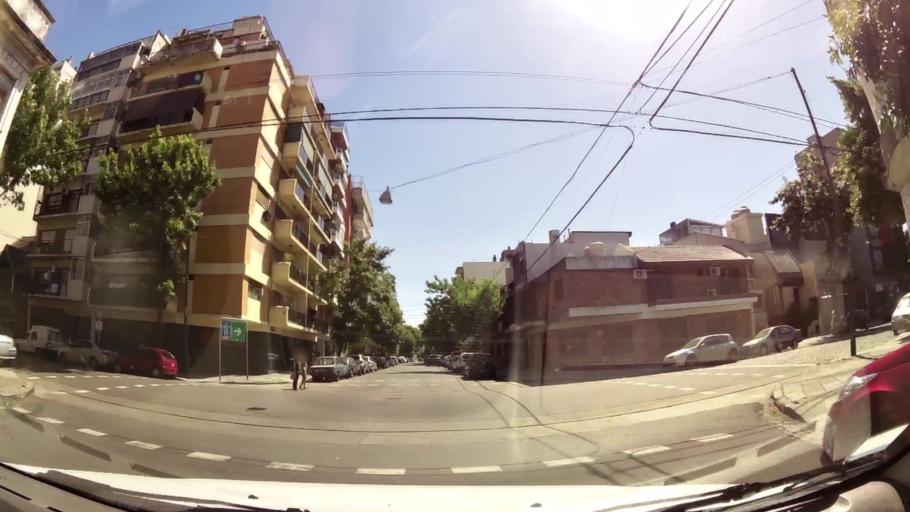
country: AR
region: Buenos Aires F.D.
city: Villa Santa Rita
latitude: -34.6326
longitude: -58.4470
